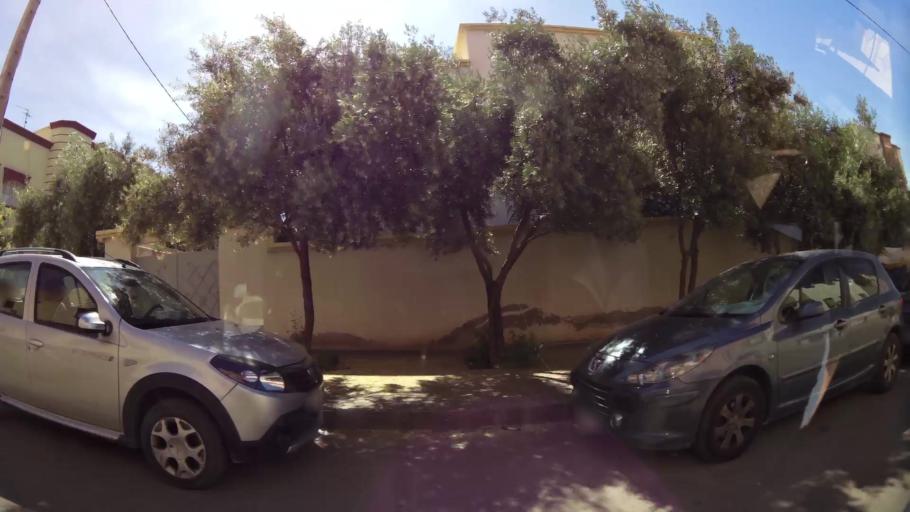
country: MA
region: Oriental
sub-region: Oujda-Angad
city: Oujda
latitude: 34.6553
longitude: -1.9041
